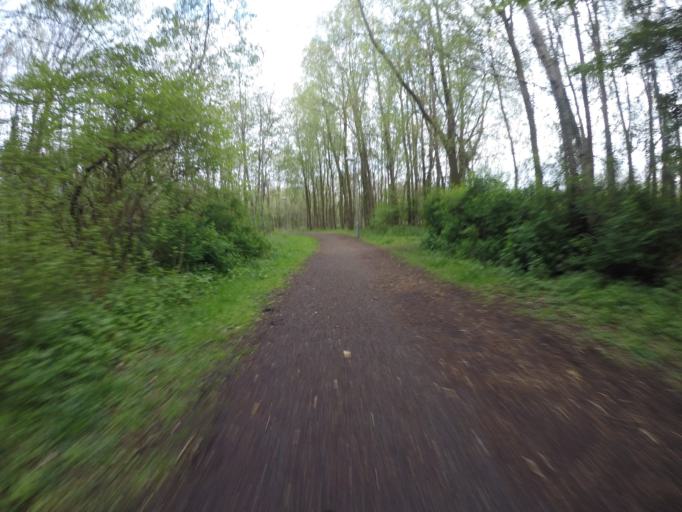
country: GB
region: Scotland
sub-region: North Ayrshire
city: Irvine
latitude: 55.6320
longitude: -4.6294
